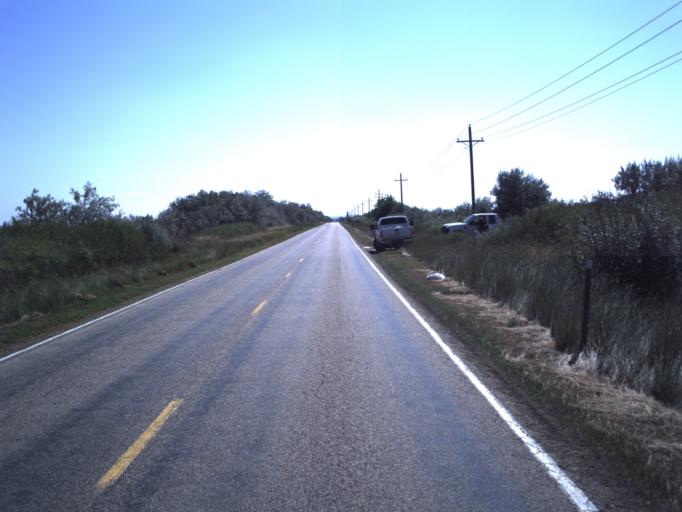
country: US
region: Utah
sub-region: Duchesne County
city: Roosevelt
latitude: 40.2580
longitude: -110.1943
